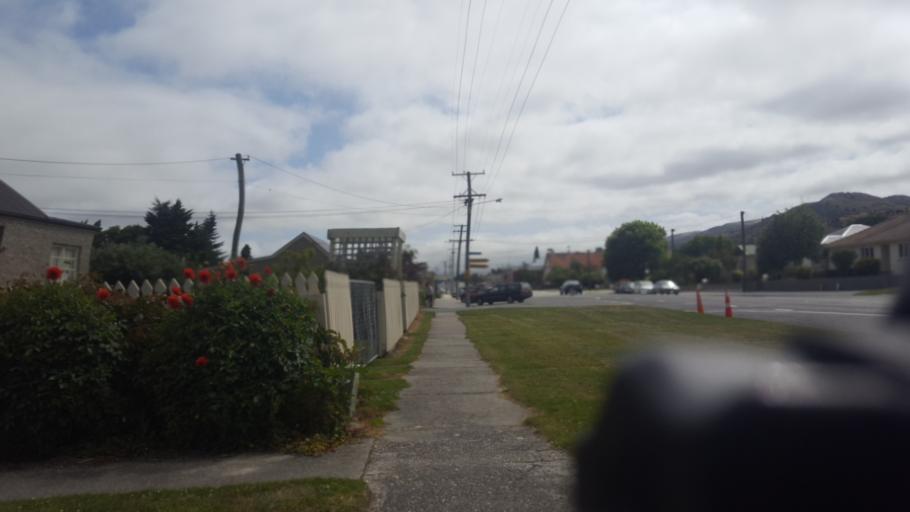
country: NZ
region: Otago
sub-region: Queenstown-Lakes District
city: Kingston
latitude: -45.5444
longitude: 169.3138
